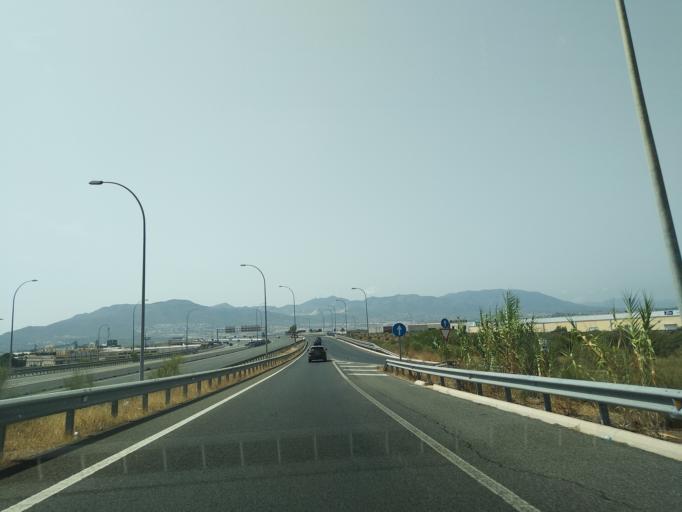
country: ES
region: Andalusia
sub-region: Provincia de Malaga
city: Alhaurin de la Torre
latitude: 36.7099
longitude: -4.5116
